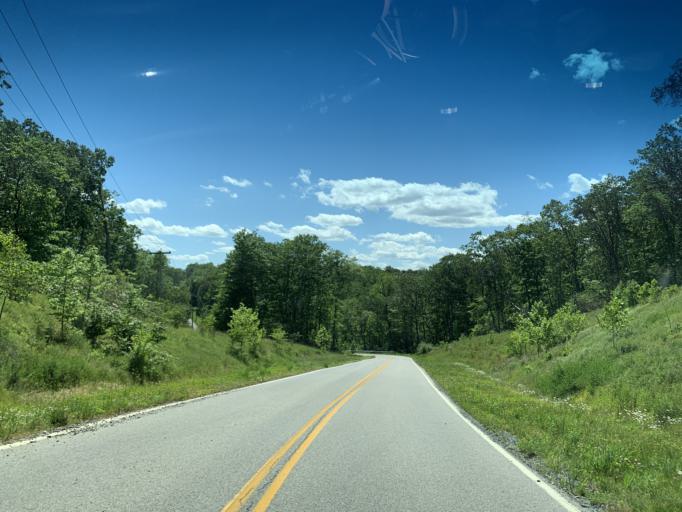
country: US
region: Maryland
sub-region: Cecil County
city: Charlestown
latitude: 39.5216
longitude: -75.9404
